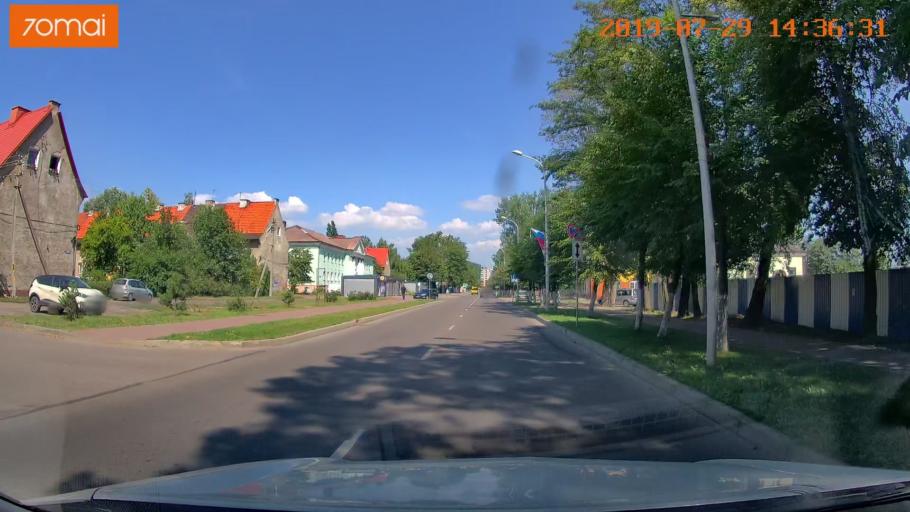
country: RU
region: Kaliningrad
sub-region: Gorod Kaliningrad
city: Baltiysk
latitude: 54.6474
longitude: 19.9007
